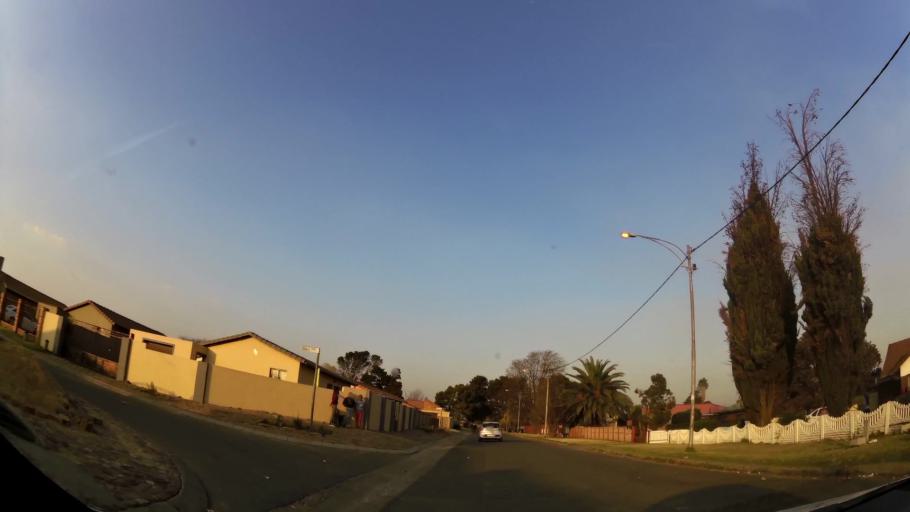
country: ZA
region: Gauteng
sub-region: Ekurhuleni Metropolitan Municipality
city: Springs
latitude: -26.2665
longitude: 28.4087
